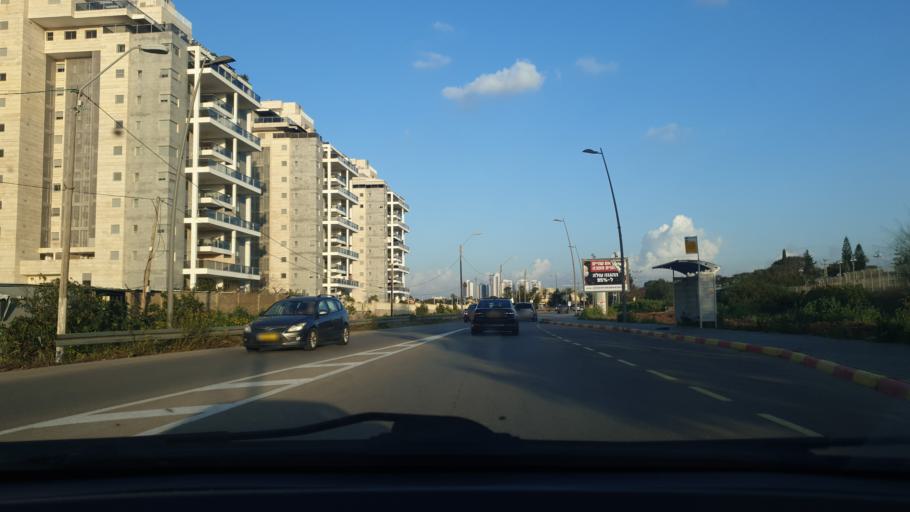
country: IL
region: Central District
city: Ness Ziona
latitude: 31.9334
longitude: 34.8268
